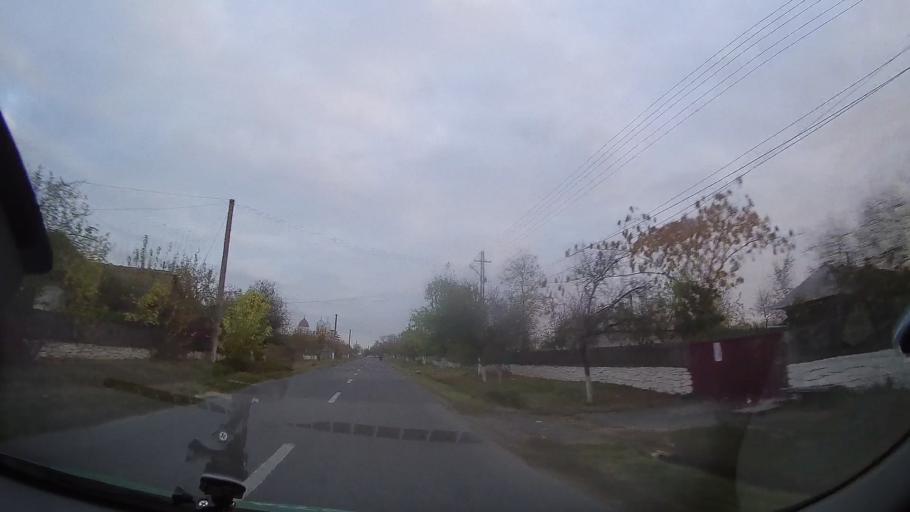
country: RO
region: Tulcea
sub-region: Comuna Mihai Bravu
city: Turda
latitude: 44.9781
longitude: 28.6186
